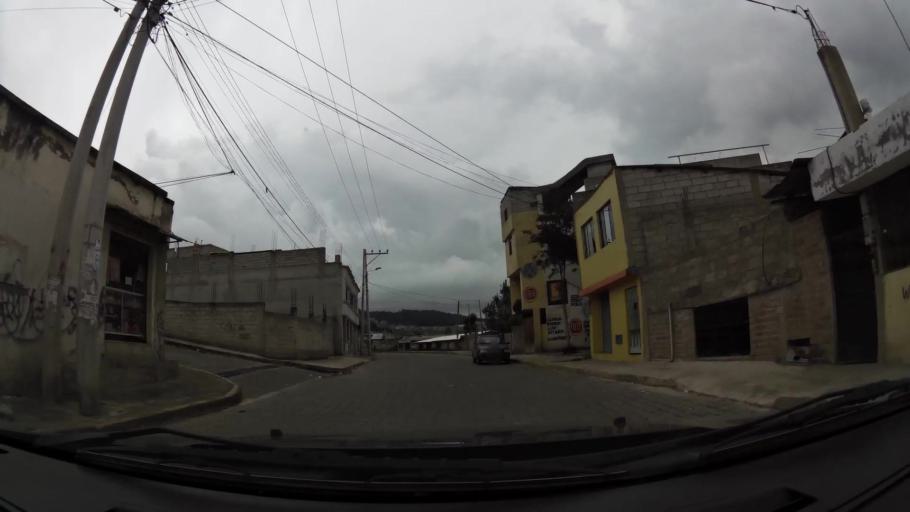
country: EC
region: Pichincha
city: Sangolqui
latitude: -0.3198
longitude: -78.5338
